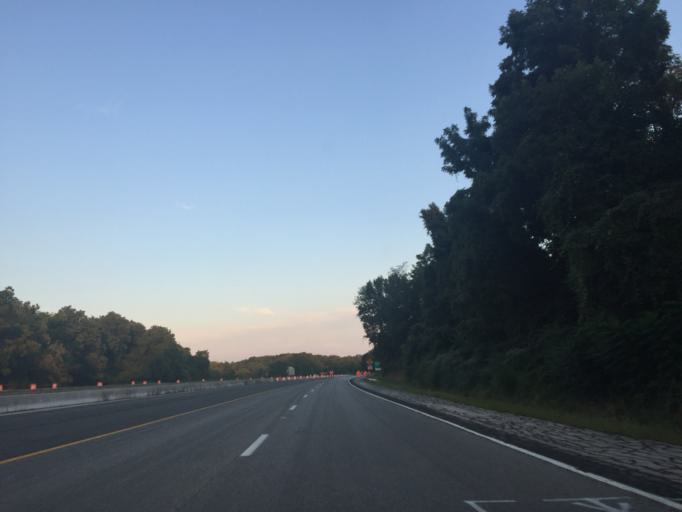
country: US
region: Maryland
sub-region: Baltimore County
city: Woodlawn
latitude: 39.3036
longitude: -76.7219
